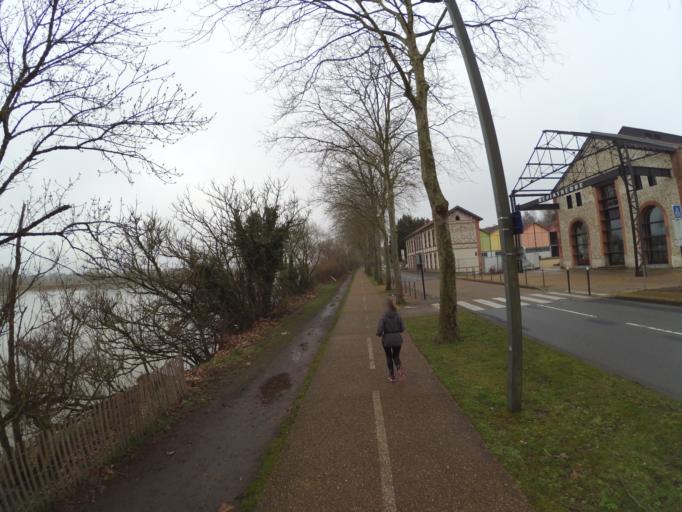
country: FR
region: Pays de la Loire
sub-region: Departement de la Loire-Atlantique
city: Coueron
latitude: 47.2085
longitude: -1.7199
